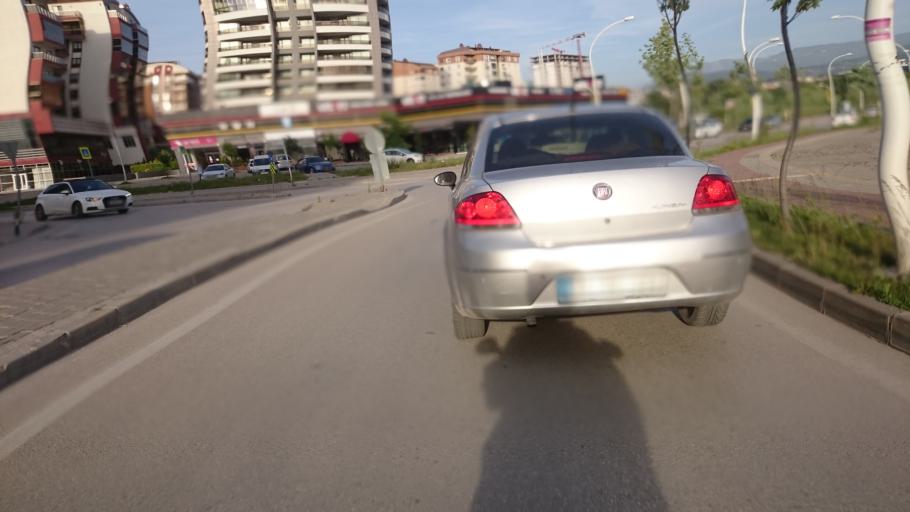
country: TR
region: Bursa
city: Cali
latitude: 40.2164
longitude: 28.9416
